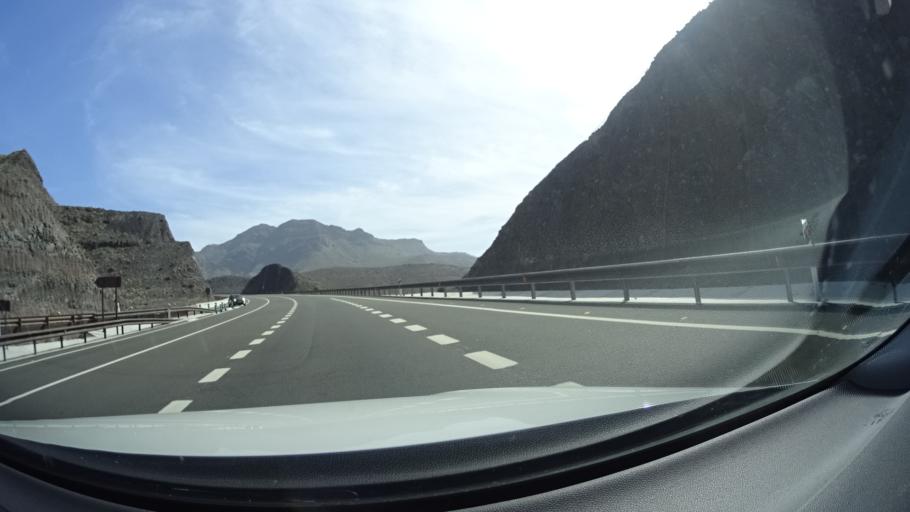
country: ES
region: Canary Islands
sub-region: Provincia de Las Palmas
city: San Nicolas
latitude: 28.0093
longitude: -15.7866
